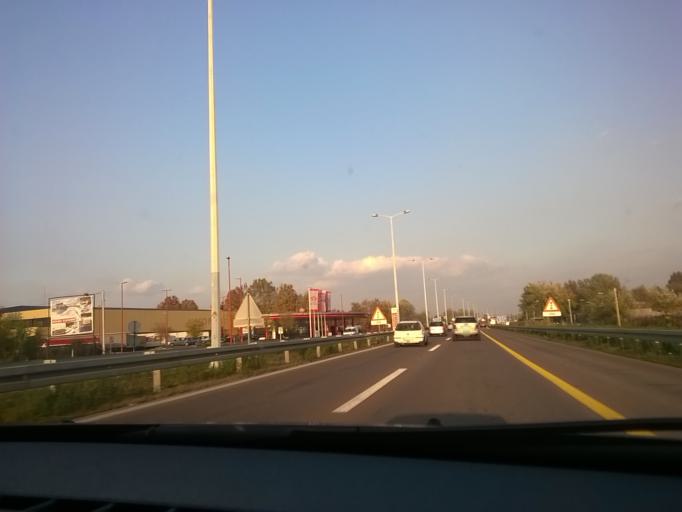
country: RS
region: Central Serbia
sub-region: Belgrade
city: Palilula
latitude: 44.8447
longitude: 20.5110
